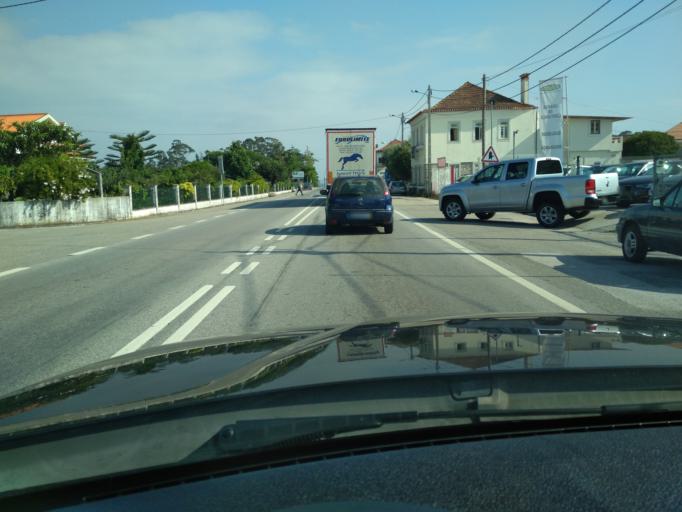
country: PT
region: Aveiro
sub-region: Mealhada
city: Pampilhosa do Botao
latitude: 40.3068
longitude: -8.4488
